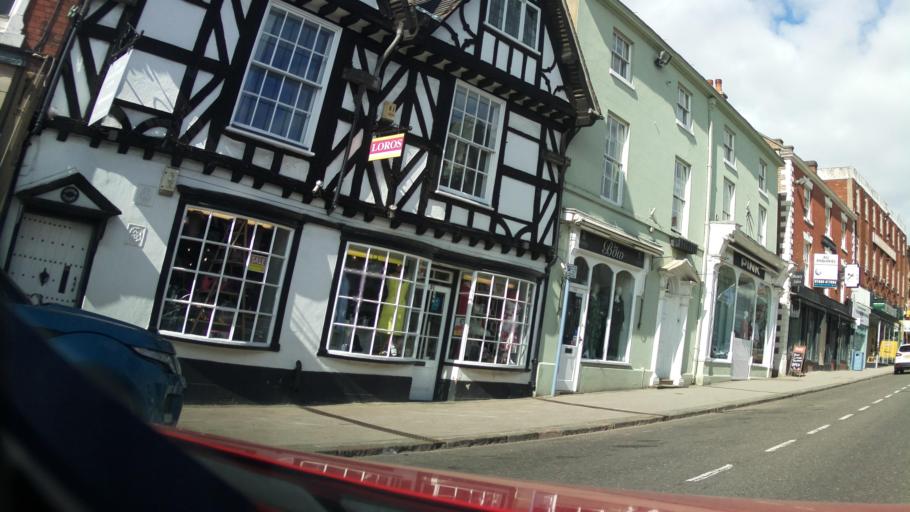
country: GB
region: England
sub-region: Leicestershire
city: Ashby de la Zouch
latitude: 52.7472
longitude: -1.4712
